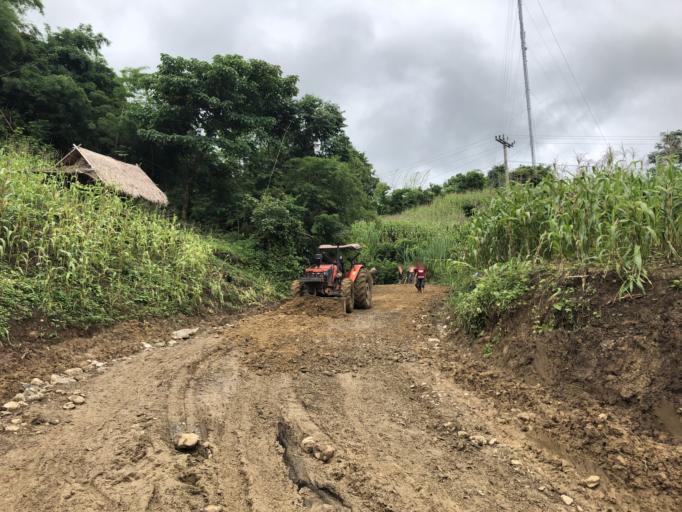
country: LA
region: Loungnamtha
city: Muang Nale
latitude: 20.0989
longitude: 101.4885
